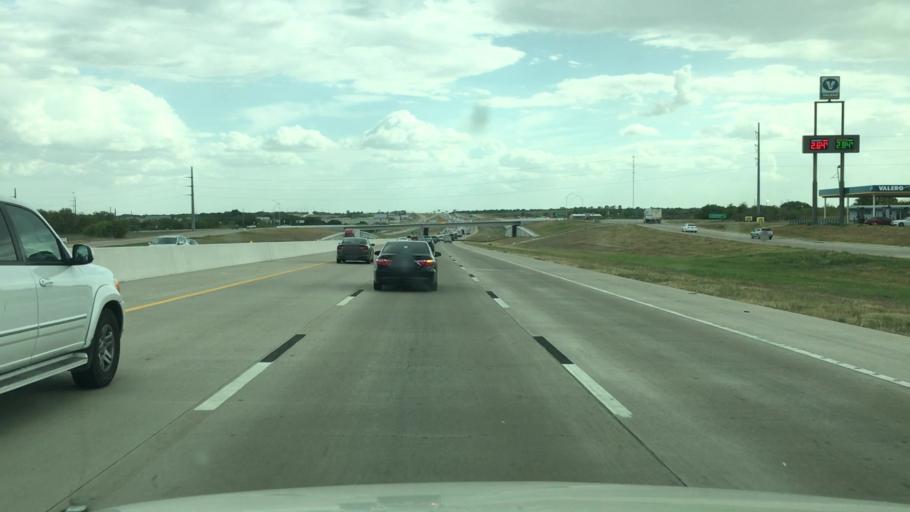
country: US
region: Texas
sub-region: McLennan County
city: Hewitt
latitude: 31.4252
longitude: -97.1922
